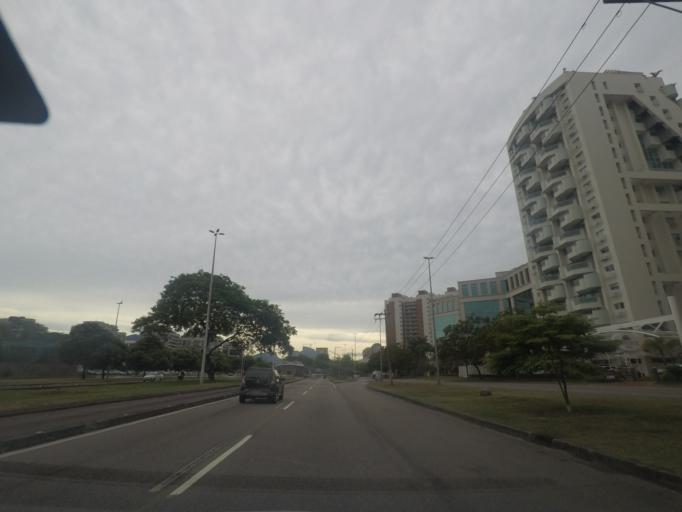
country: BR
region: Rio de Janeiro
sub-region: Nilopolis
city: Nilopolis
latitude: -23.0005
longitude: -43.3918
